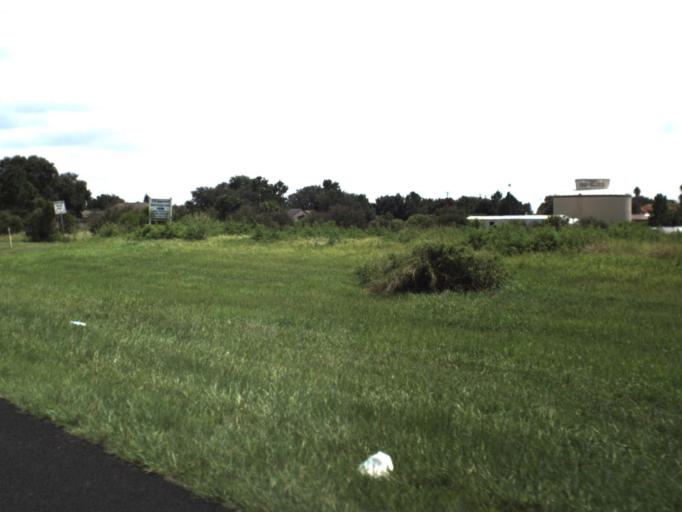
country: US
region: Florida
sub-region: Polk County
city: Cypress Gardens
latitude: 27.9800
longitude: -81.6695
